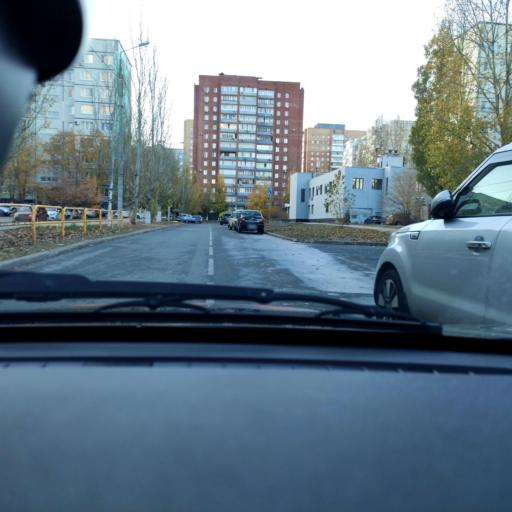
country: RU
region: Samara
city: Zhigulevsk
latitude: 53.4781
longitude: 49.4606
